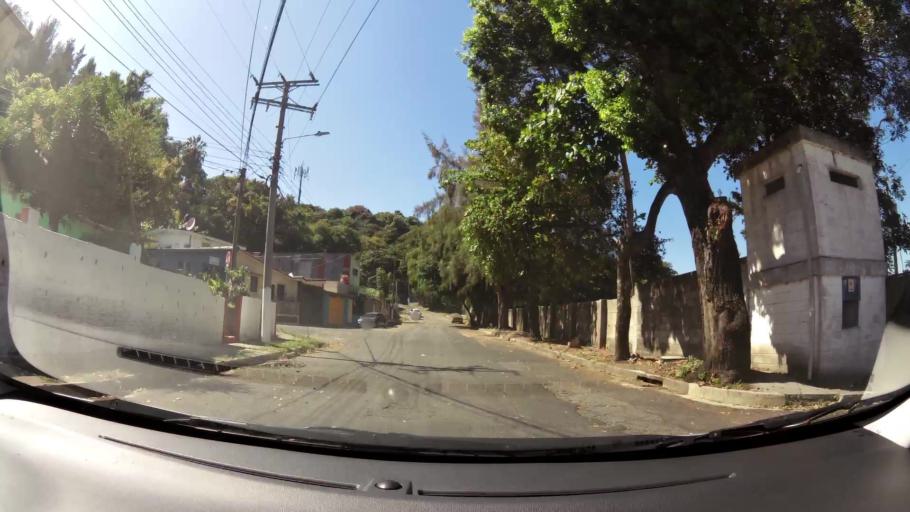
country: SV
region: La Libertad
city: Santa Tecla
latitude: 13.6727
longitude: -89.3028
